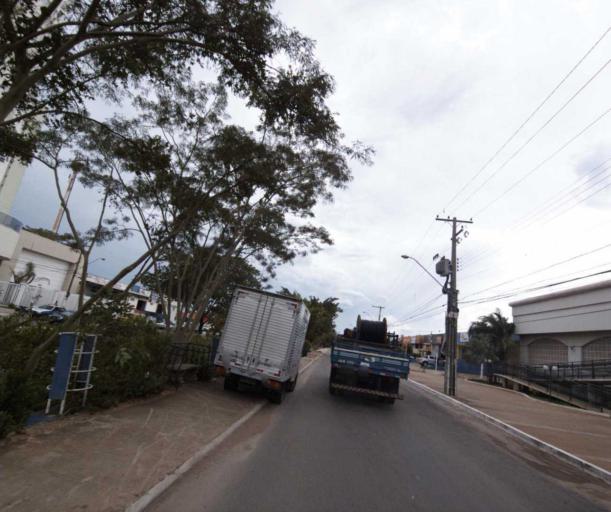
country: BR
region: Mato Grosso
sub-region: Cuiaba
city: Cuiaba
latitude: -15.6140
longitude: -56.0753
